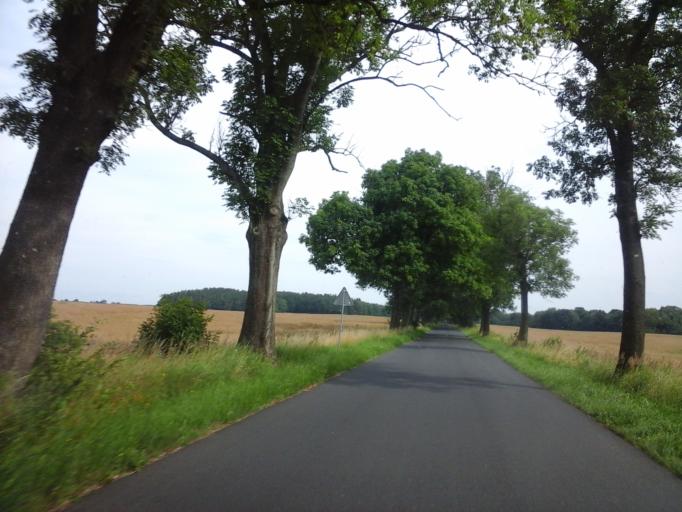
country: PL
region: West Pomeranian Voivodeship
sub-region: Powiat choszczenski
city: Recz
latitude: 53.2305
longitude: 15.6042
